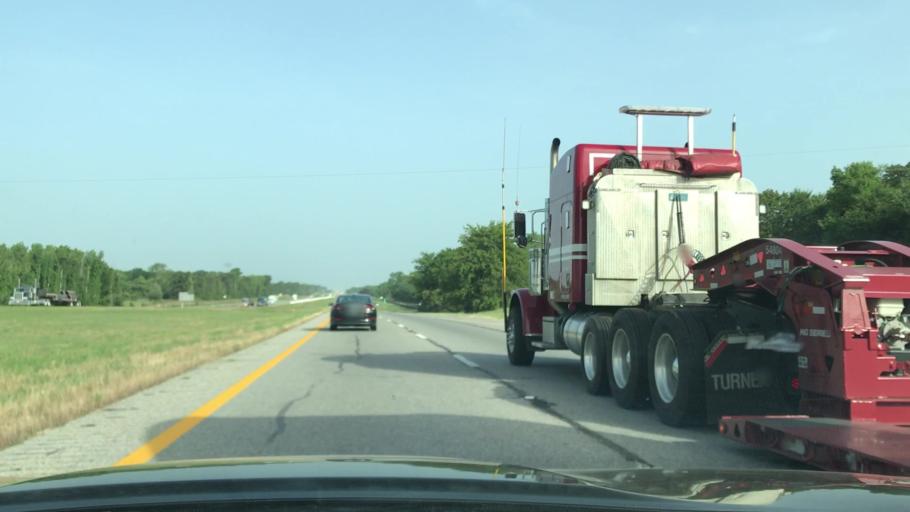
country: US
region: Texas
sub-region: Van Zandt County
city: Van
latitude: 32.5287
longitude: -95.7185
